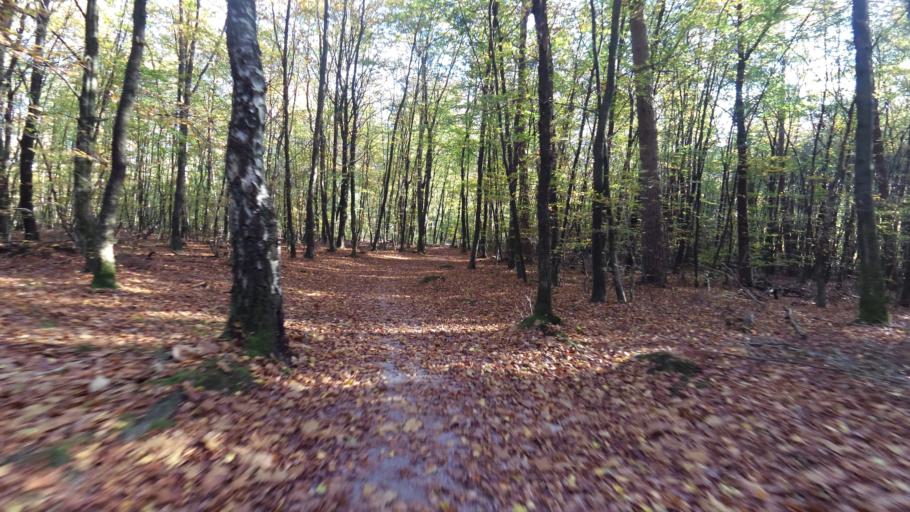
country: NL
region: Gelderland
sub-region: Gemeente Epe
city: Epe
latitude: 52.3657
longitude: 5.9666
